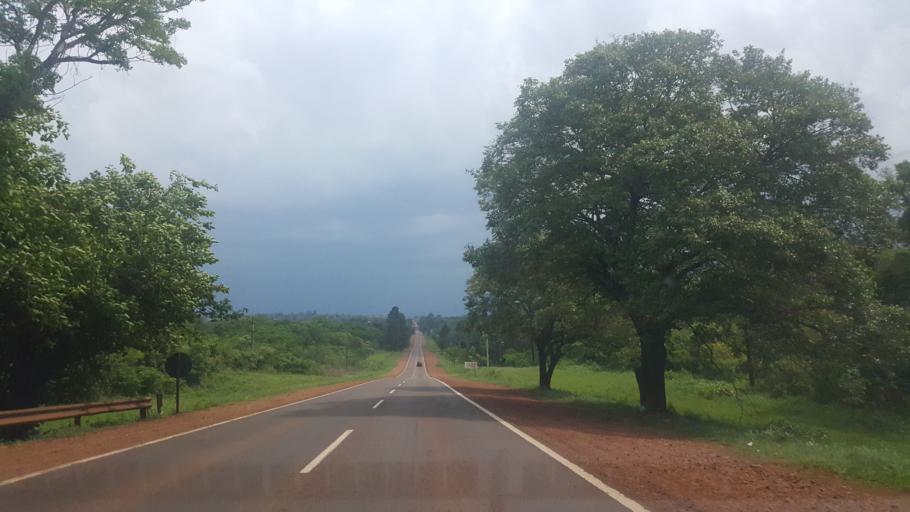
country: AR
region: Misiones
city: Gobernador Roca
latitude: -27.1711
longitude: -55.4473
